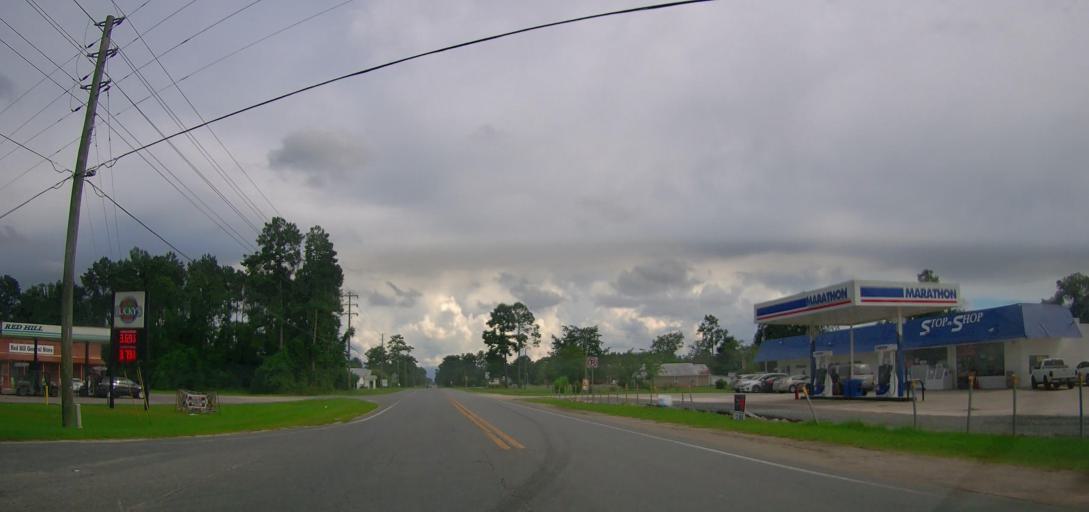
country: US
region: Georgia
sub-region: Wayne County
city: Jesup
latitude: 31.6585
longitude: -81.9135
